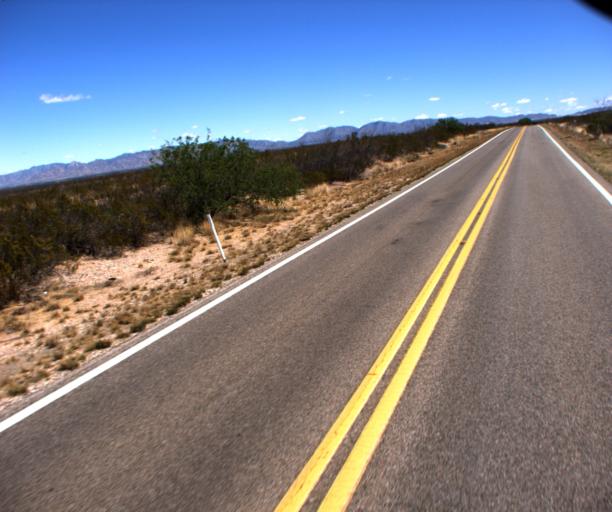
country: US
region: Arizona
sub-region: Cochise County
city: Tombstone
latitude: 31.7438
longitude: -110.1513
